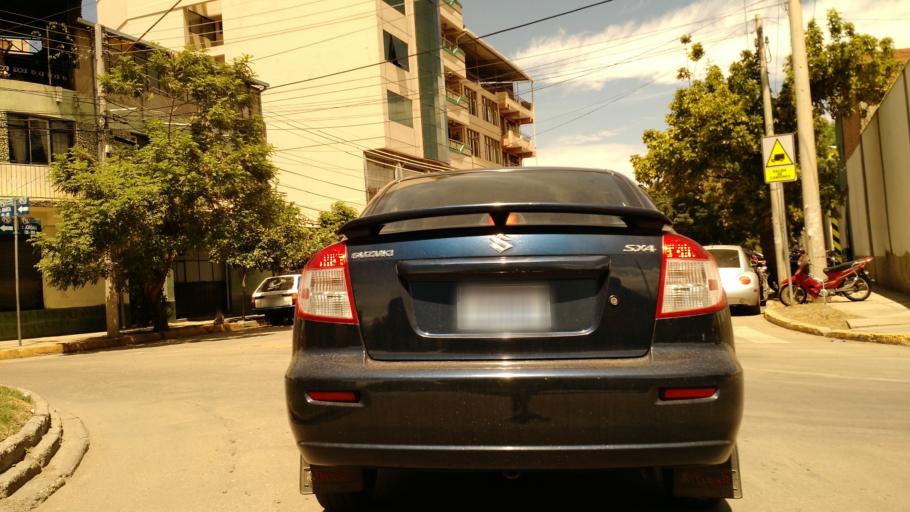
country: BO
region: Cochabamba
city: Cochabamba
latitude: -17.3967
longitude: -66.1657
